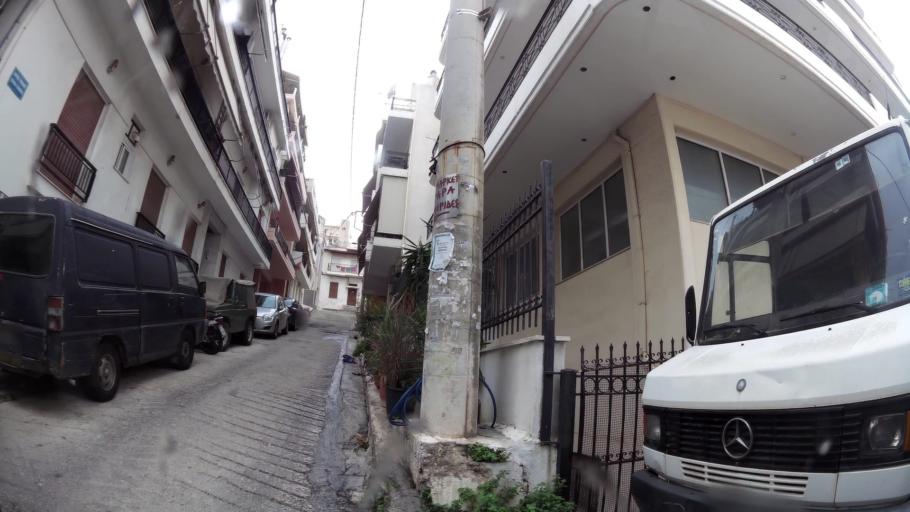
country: GR
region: Attica
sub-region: Nomos Piraios
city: Nikaia
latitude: 37.9614
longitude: 23.6463
